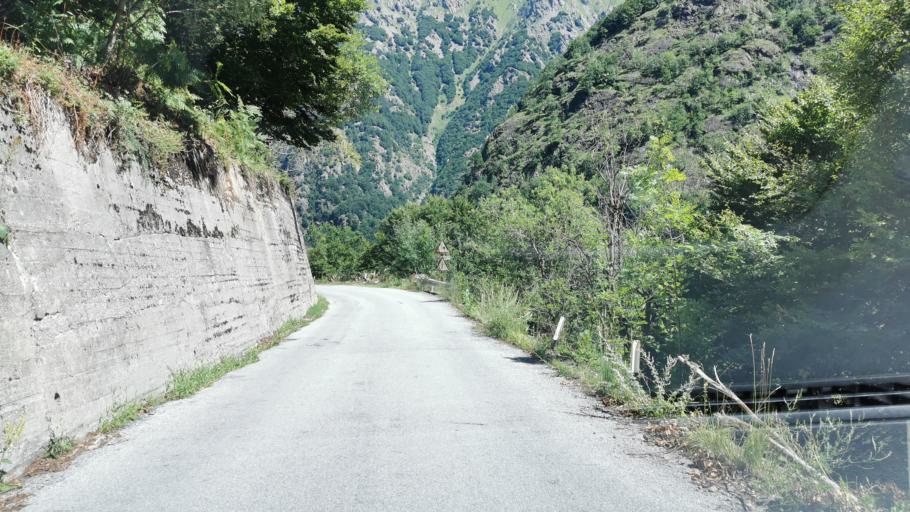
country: IT
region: Piedmont
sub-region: Provincia di Cuneo
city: Entracque
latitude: 44.2032
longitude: 7.3678
